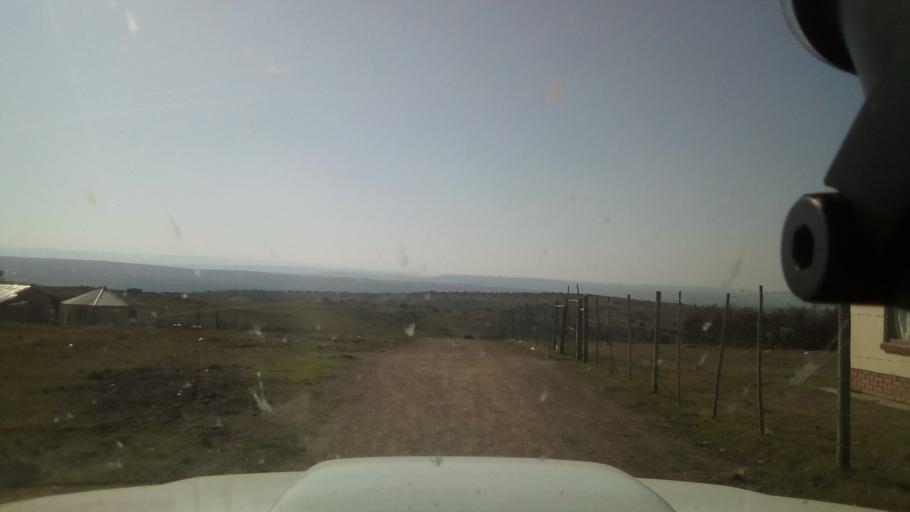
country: ZA
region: Eastern Cape
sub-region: Buffalo City Metropolitan Municipality
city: Bhisho
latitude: -32.9398
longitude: 27.3397
